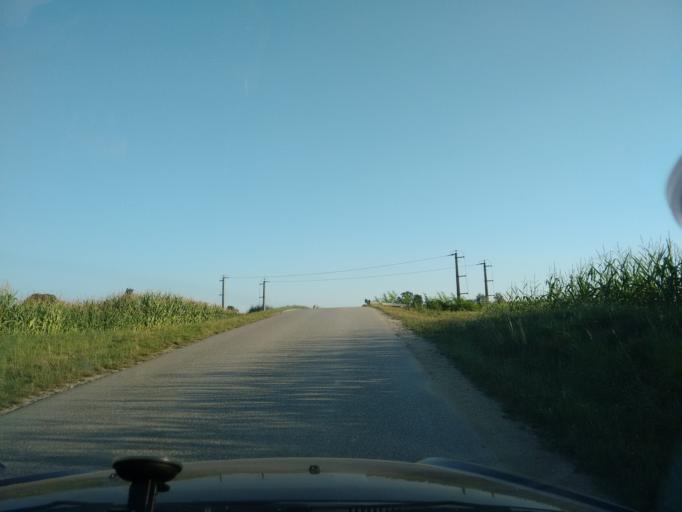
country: AT
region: Upper Austria
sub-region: Politischer Bezirk Grieskirchen
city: Bad Schallerbach
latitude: 48.2161
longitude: 13.9473
